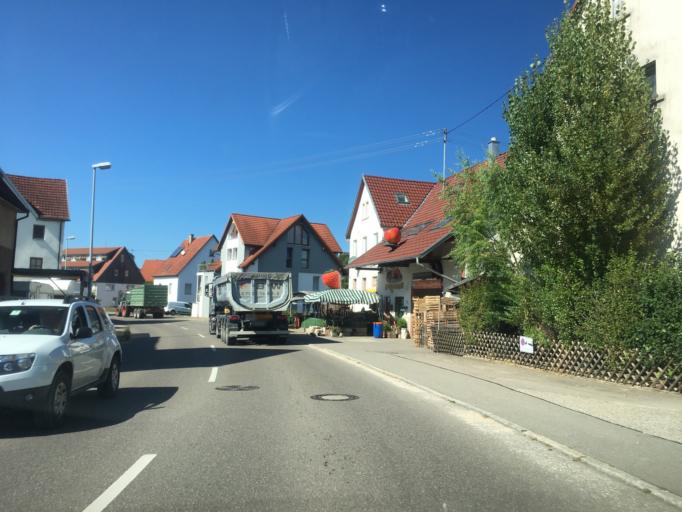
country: DE
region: Baden-Wuerttemberg
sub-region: Tuebingen Region
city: Sankt Johann
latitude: 48.3851
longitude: 9.3020
